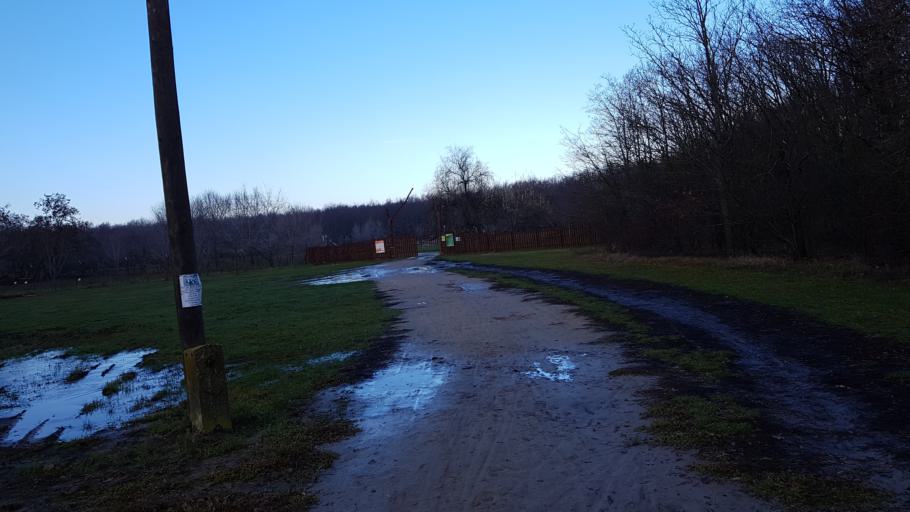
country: HU
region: Jasz-Nagykun-Szolnok
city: Szolnok
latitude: 47.2026
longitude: 20.1930
